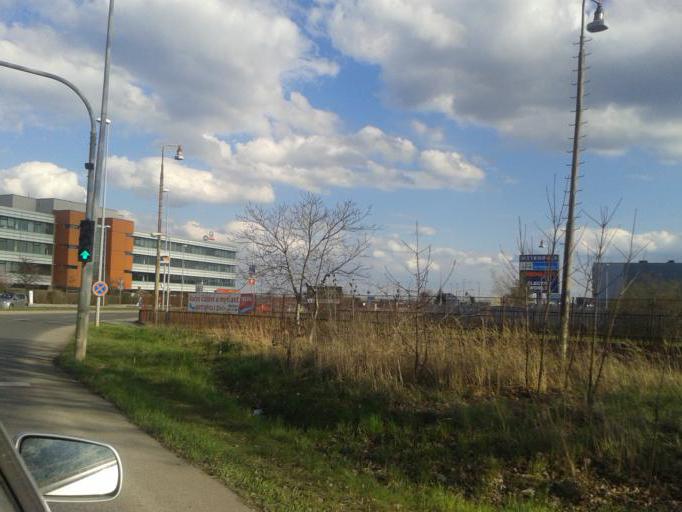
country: CZ
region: Central Bohemia
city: Hostivice
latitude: 50.0563
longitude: 14.2866
